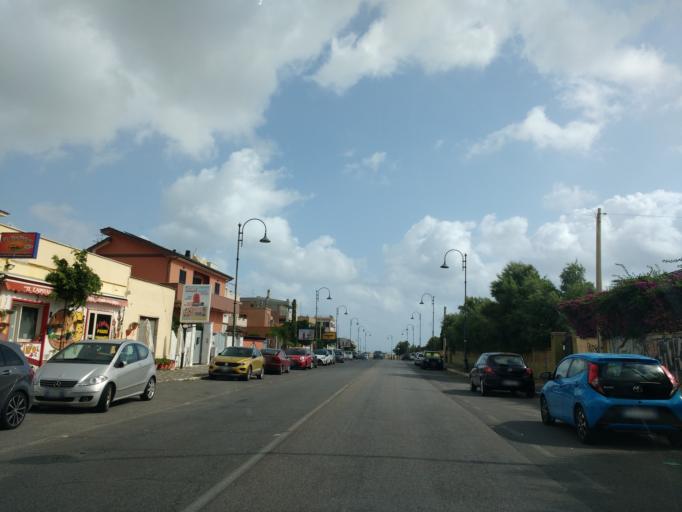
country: IT
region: Latium
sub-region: Citta metropolitana di Roma Capitale
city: Anzio
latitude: 41.4644
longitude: 12.6111
